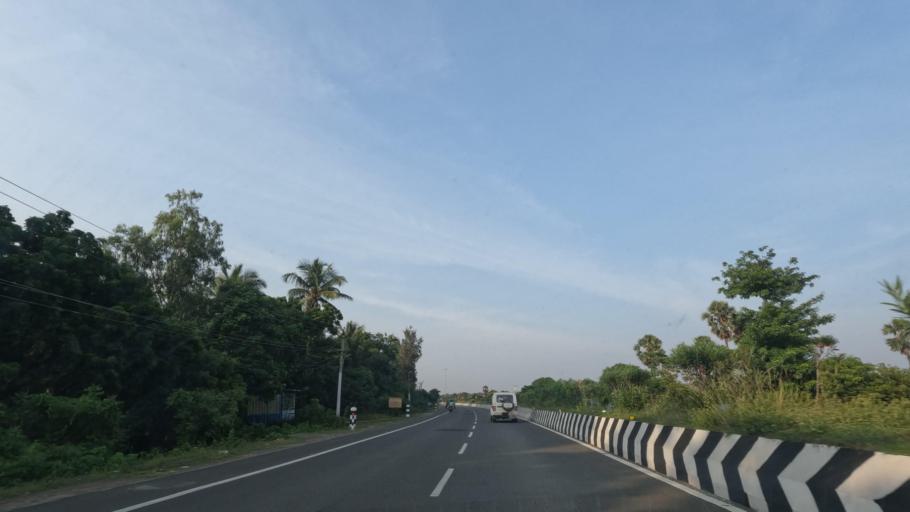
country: IN
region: Tamil Nadu
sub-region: Kancheepuram
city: Mamallapuram
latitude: 12.6579
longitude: 80.2083
